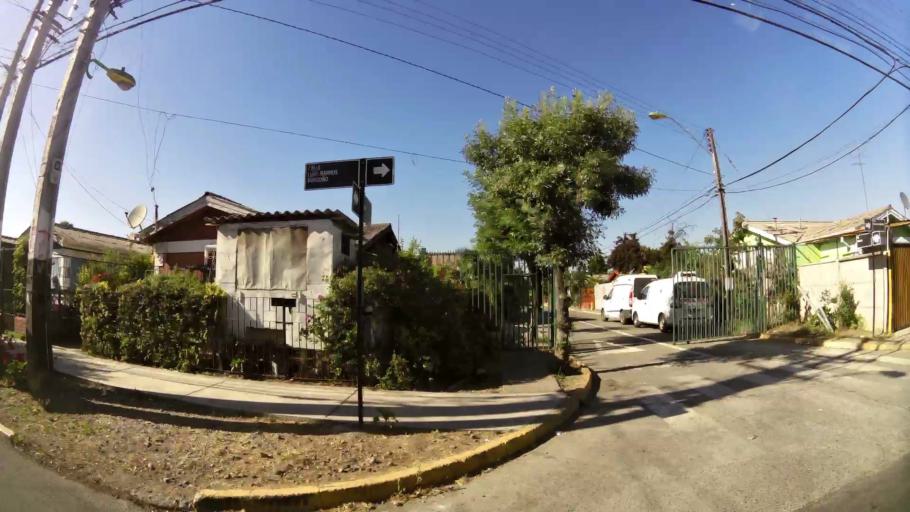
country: CL
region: Santiago Metropolitan
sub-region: Provincia de Maipo
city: San Bernardo
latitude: -33.5515
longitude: -70.6780
